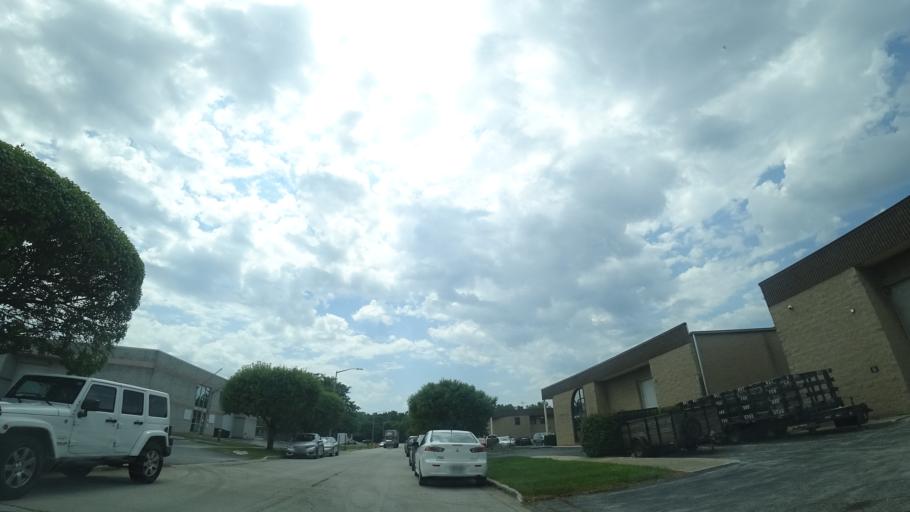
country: US
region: Illinois
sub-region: Cook County
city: Crestwood
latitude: 41.6637
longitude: -87.7462
